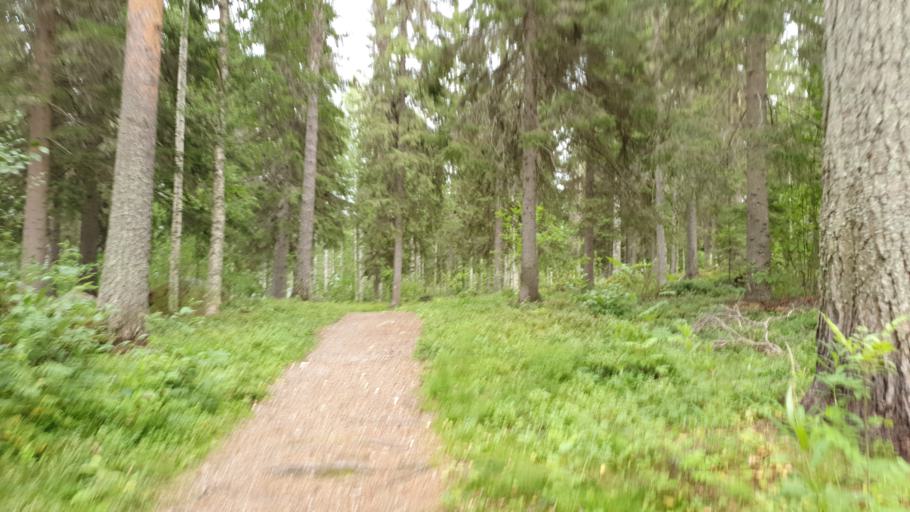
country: FI
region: Kainuu
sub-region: Kehys-Kainuu
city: Kuhmo
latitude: 64.1376
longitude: 29.4606
